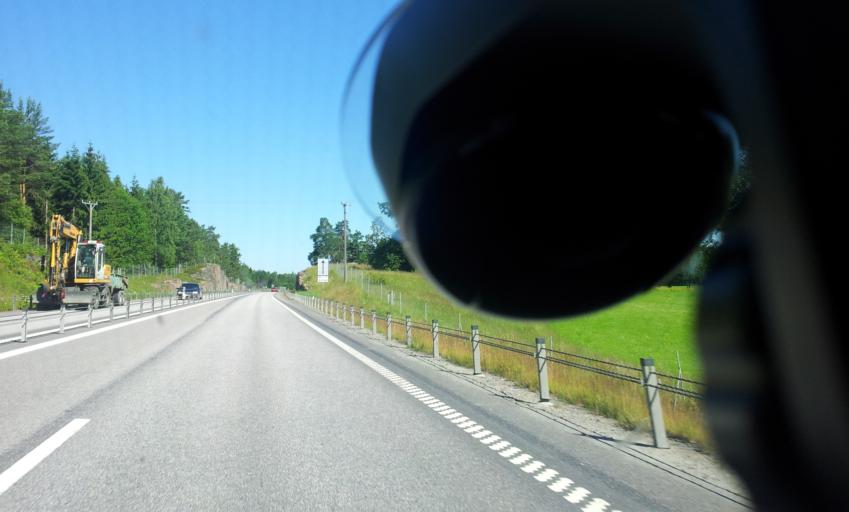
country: SE
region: OEstergoetland
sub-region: Valdemarsviks Kommun
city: Gusum
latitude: 58.3633
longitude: 16.4341
